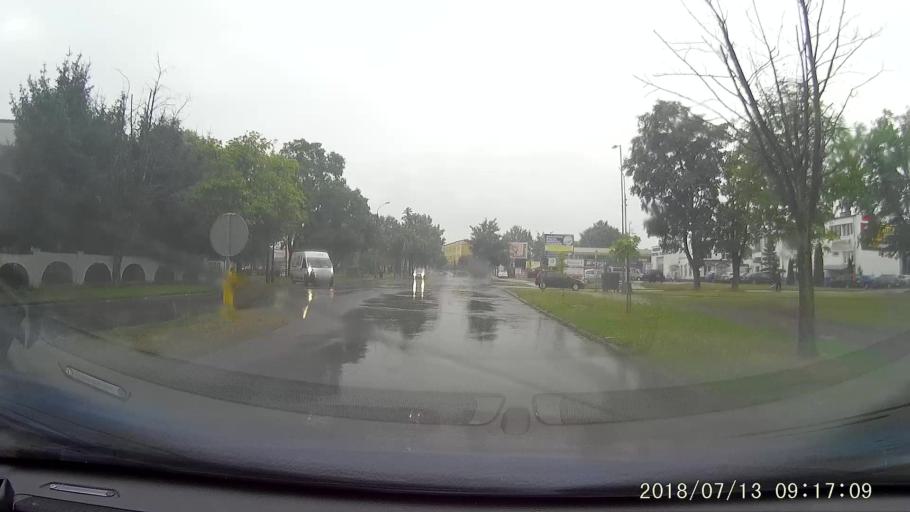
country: PL
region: Lower Silesian Voivodeship
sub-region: Powiat lubanski
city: Luban
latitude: 51.1256
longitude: 15.2885
